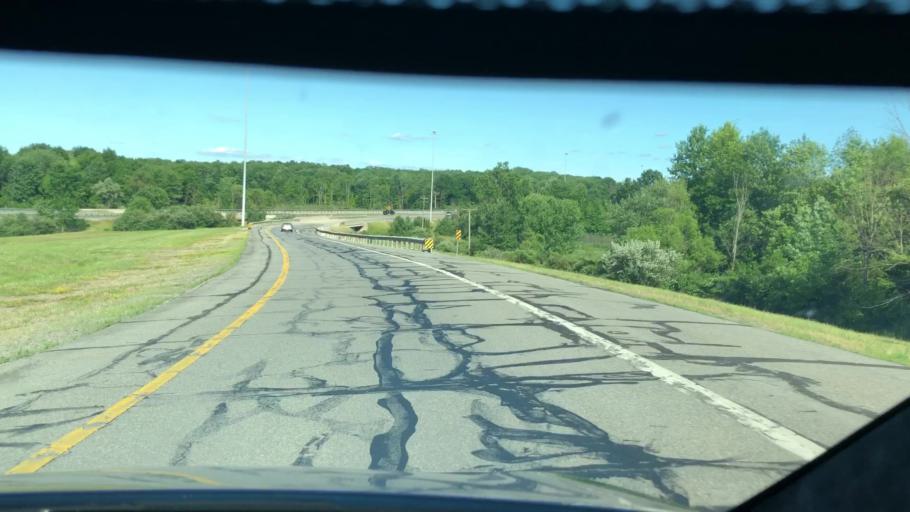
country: US
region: Ohio
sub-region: Mahoning County
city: Poland
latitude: 40.9521
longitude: -80.6378
